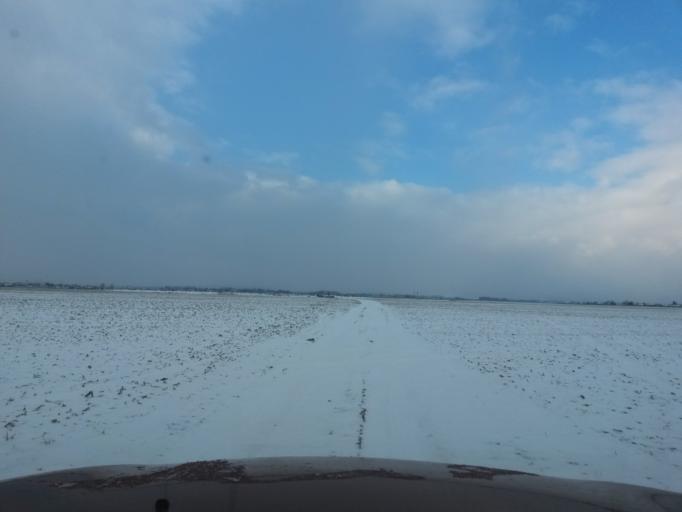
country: SK
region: Kosicky
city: Kosice
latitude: 48.6317
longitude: 21.3421
